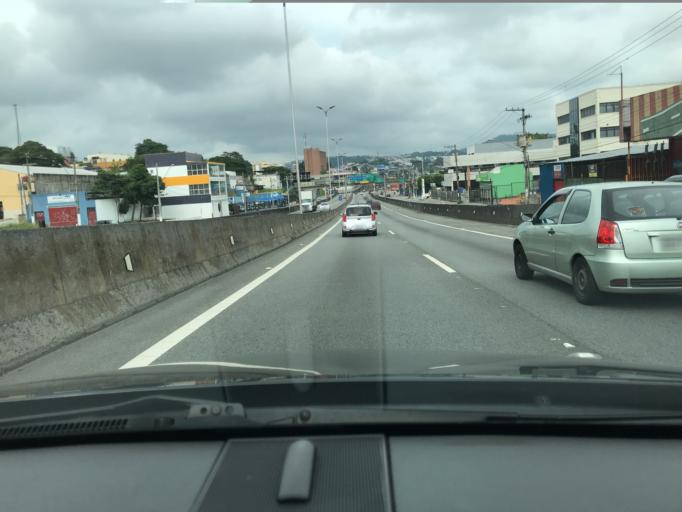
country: BR
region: Sao Paulo
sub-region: Cotia
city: Cotia
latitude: -23.6019
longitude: -46.9099
